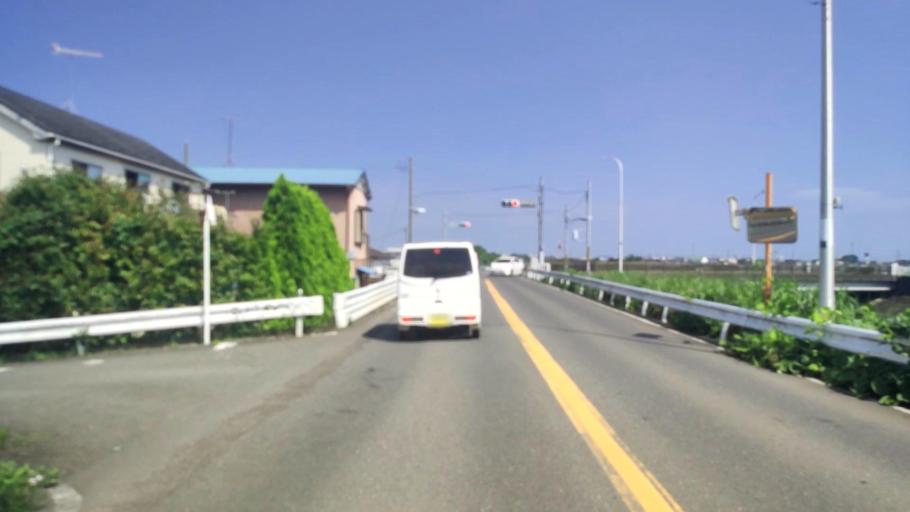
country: JP
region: Kanagawa
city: Isehara
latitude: 35.3674
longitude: 139.3165
